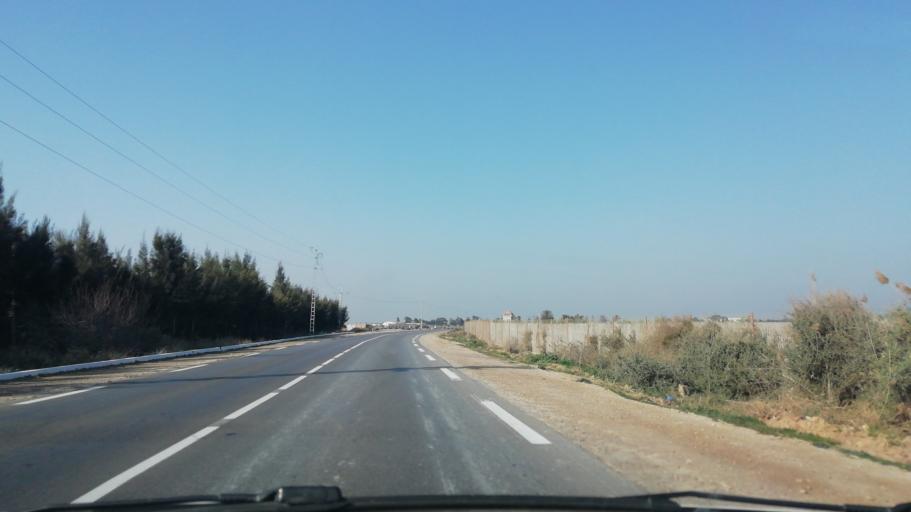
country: DZ
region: Mostaganem
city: Mostaganem
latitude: 35.7420
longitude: 0.0075
